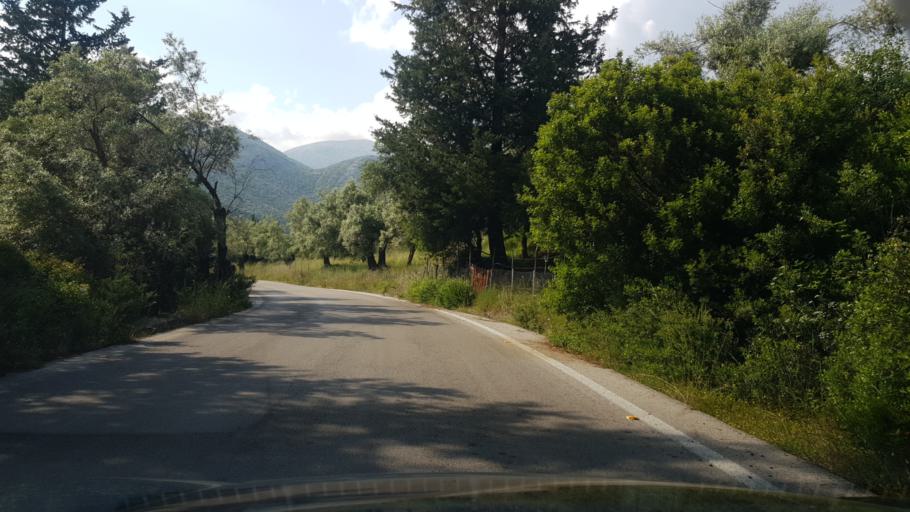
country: GR
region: Ionian Islands
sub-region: Lefkada
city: Nidri
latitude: 38.6542
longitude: 20.7029
